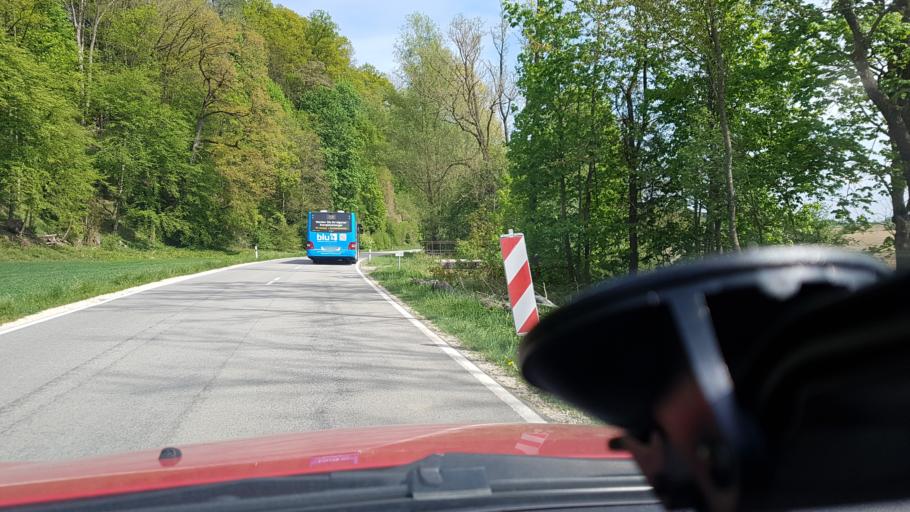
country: DE
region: Bavaria
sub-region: Lower Bavaria
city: Stubenberg
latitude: 48.3283
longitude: 13.1175
